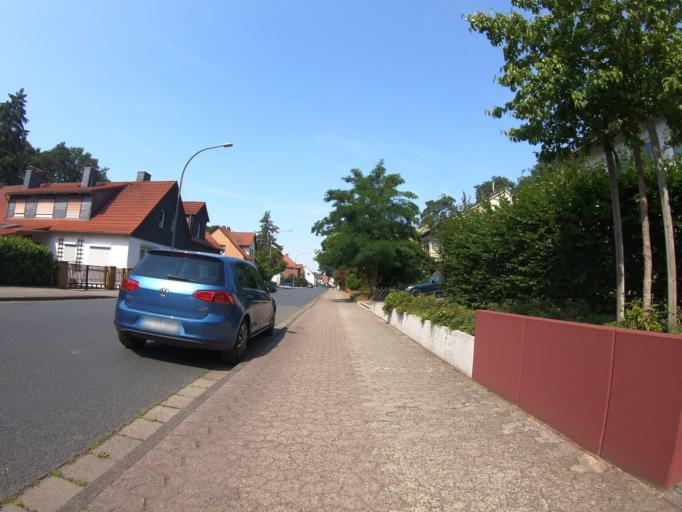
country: DE
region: Lower Saxony
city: Gifhorn
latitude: 52.4789
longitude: 10.5565
